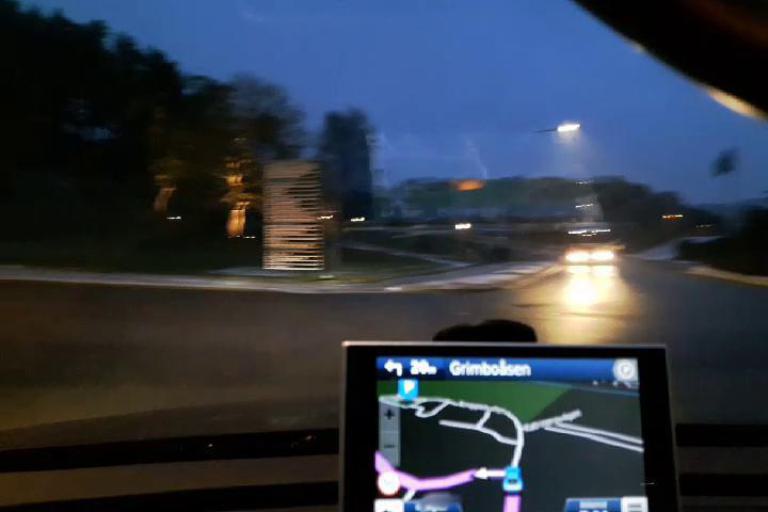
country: SE
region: Vaestra Goetaland
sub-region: Goteborg
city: Goeteborg
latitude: 57.7440
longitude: 11.9418
